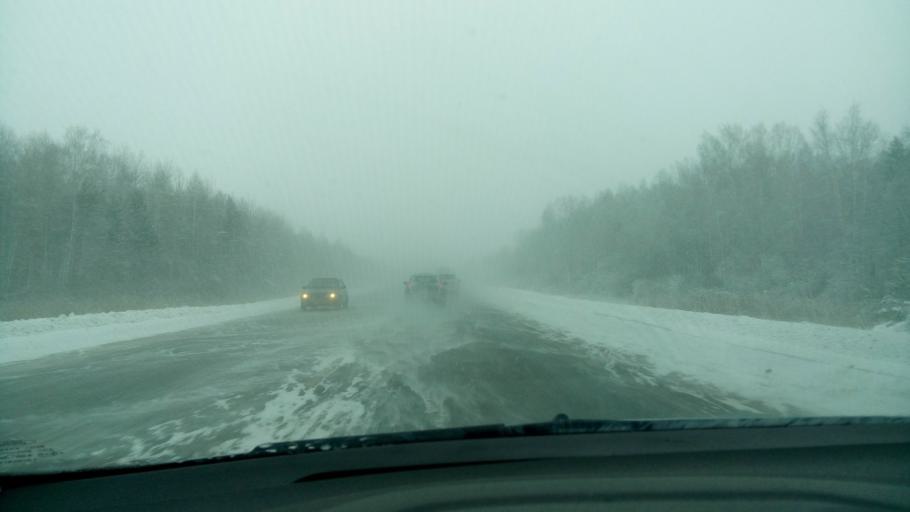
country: RU
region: Sverdlovsk
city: Bogdanovich
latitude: 56.7749
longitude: 61.9689
